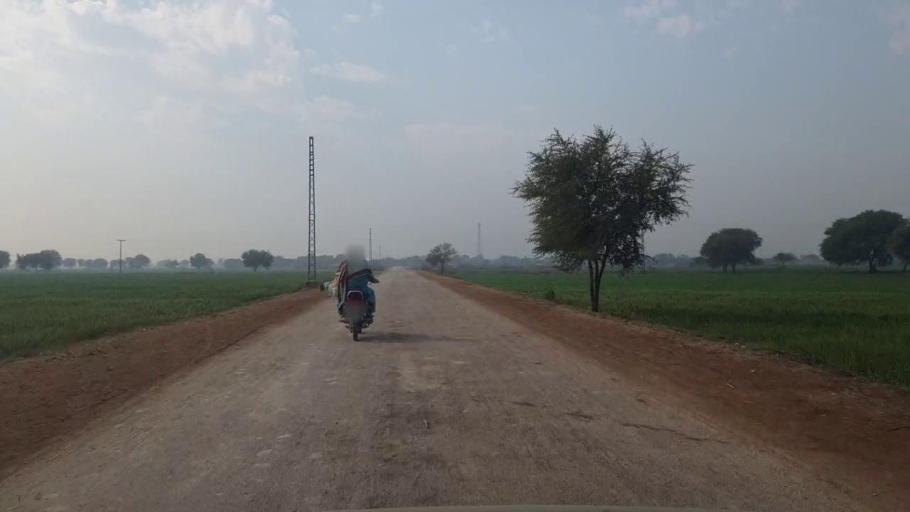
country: PK
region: Sindh
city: Hala
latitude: 25.8990
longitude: 68.4101
